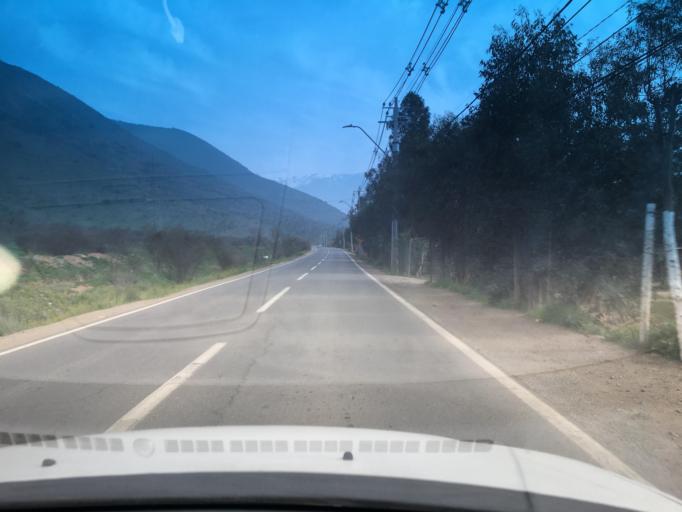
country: CL
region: Santiago Metropolitan
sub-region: Provincia de Chacabuco
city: Lampa
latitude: -33.2705
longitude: -70.8930
